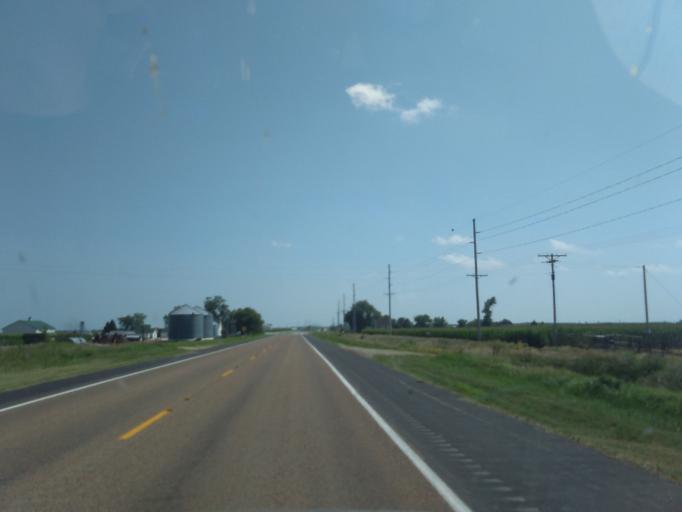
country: US
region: Nebraska
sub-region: Phelps County
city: Holdrege
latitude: 40.6646
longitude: -99.3804
